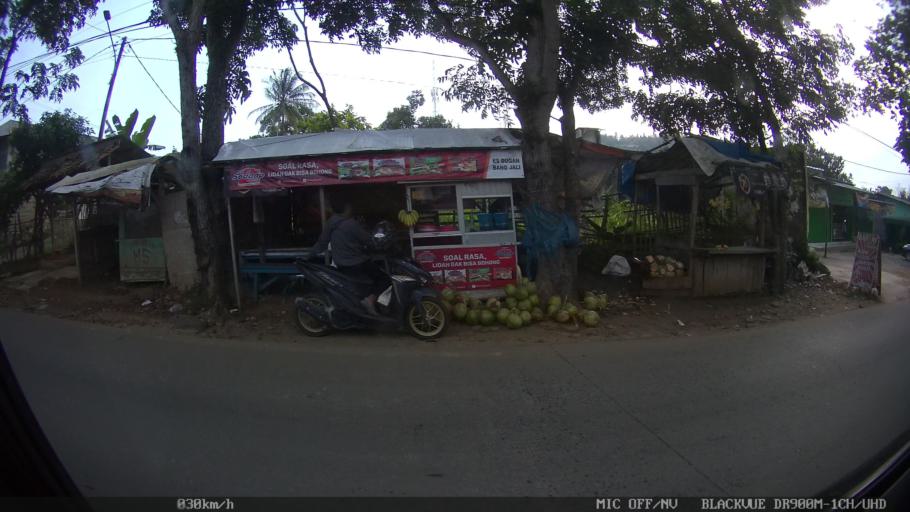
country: ID
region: Lampung
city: Bandarlampung
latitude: -5.4077
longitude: 105.2204
